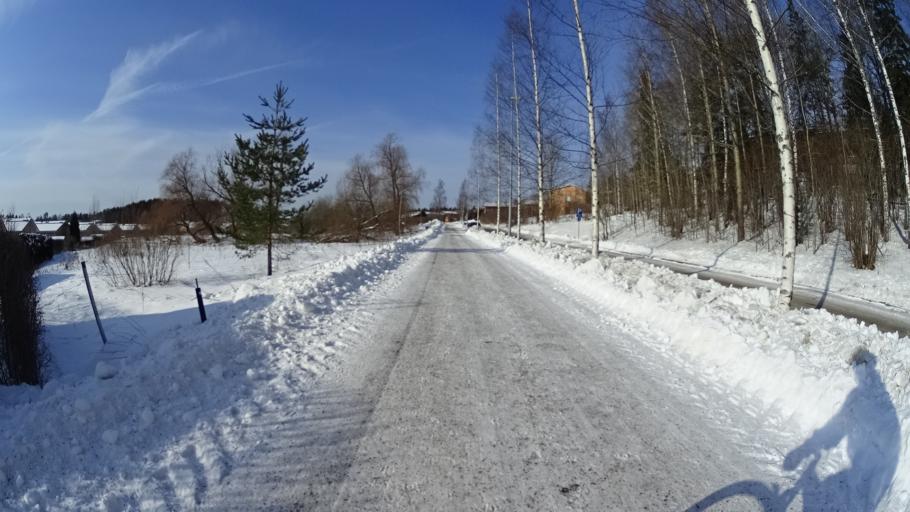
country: FI
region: Uusimaa
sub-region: Helsinki
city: Kauniainen
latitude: 60.2489
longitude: 24.7283
